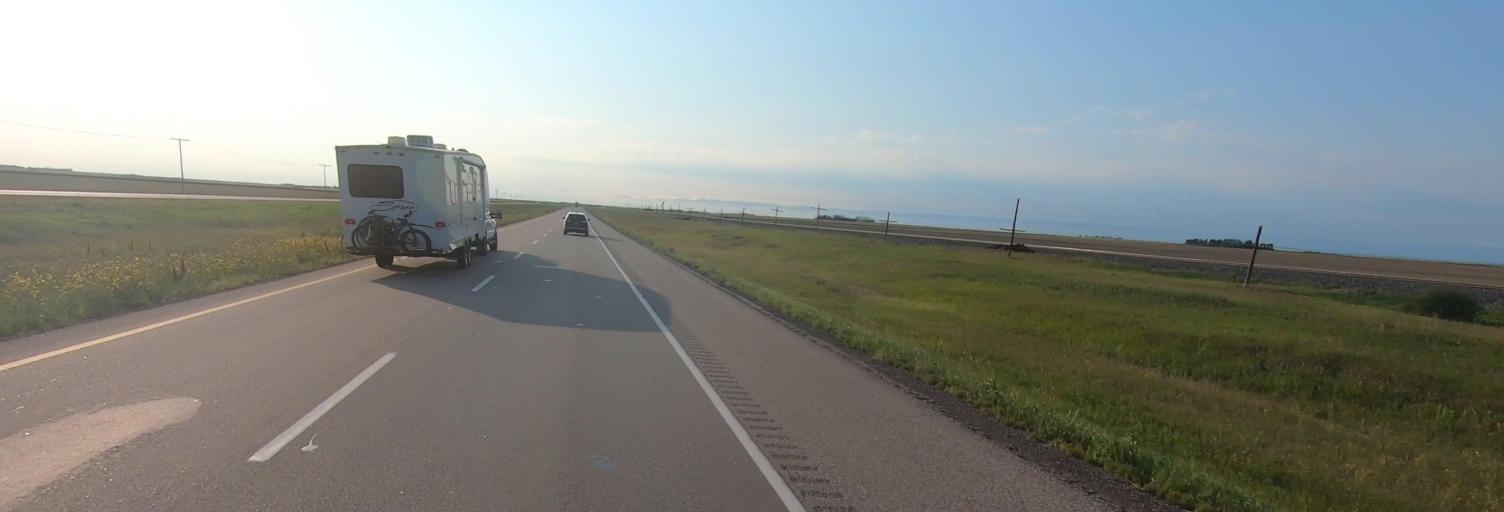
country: CA
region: Saskatchewan
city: Indian Head
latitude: 50.4882
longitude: -103.4853
